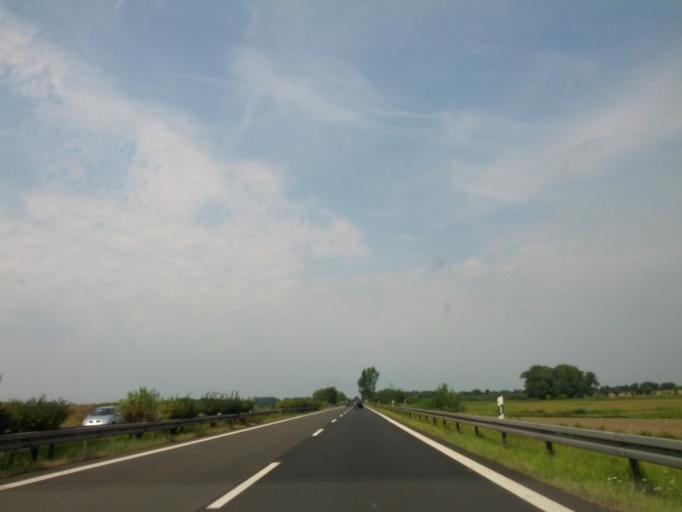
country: DE
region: Brandenburg
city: Wustermark
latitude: 52.4950
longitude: 12.9625
